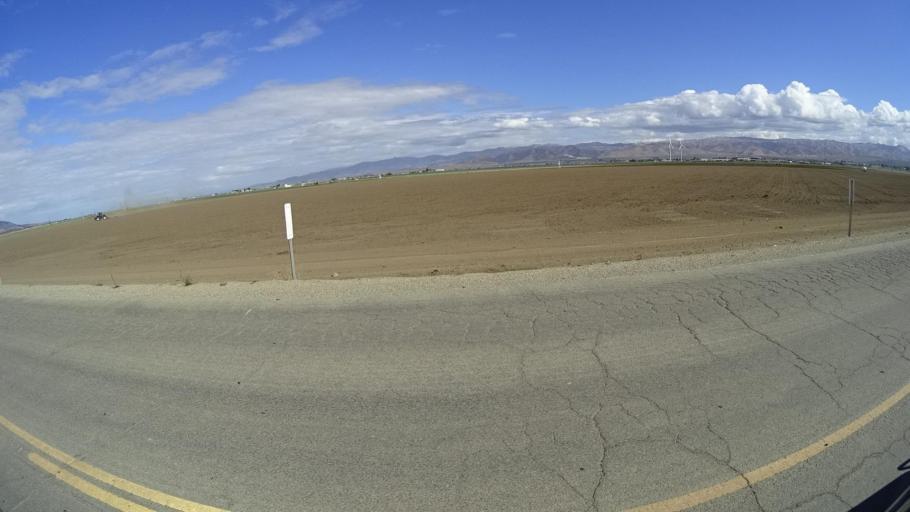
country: US
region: California
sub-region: Monterey County
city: Gonzales
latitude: 36.4887
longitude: -121.4667
